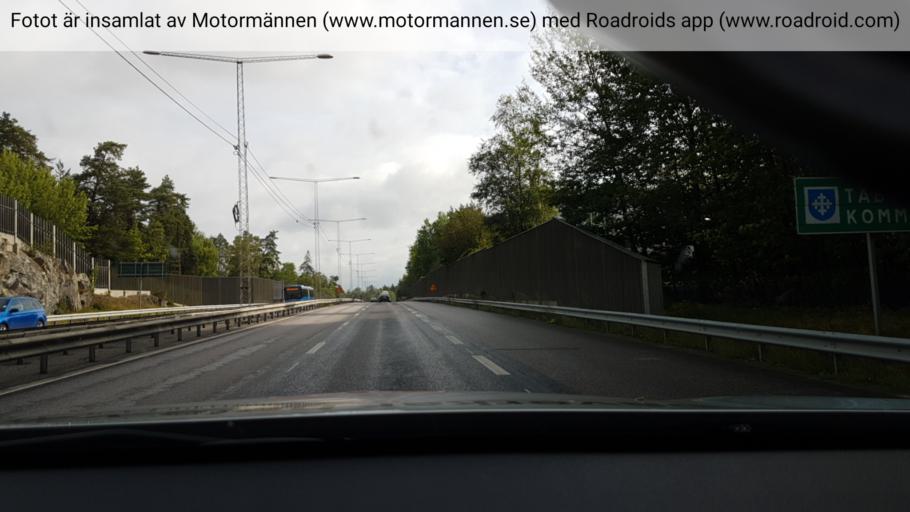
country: SE
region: Stockholm
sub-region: Danderyds Kommun
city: Djursholm
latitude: 59.4234
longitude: 18.0555
